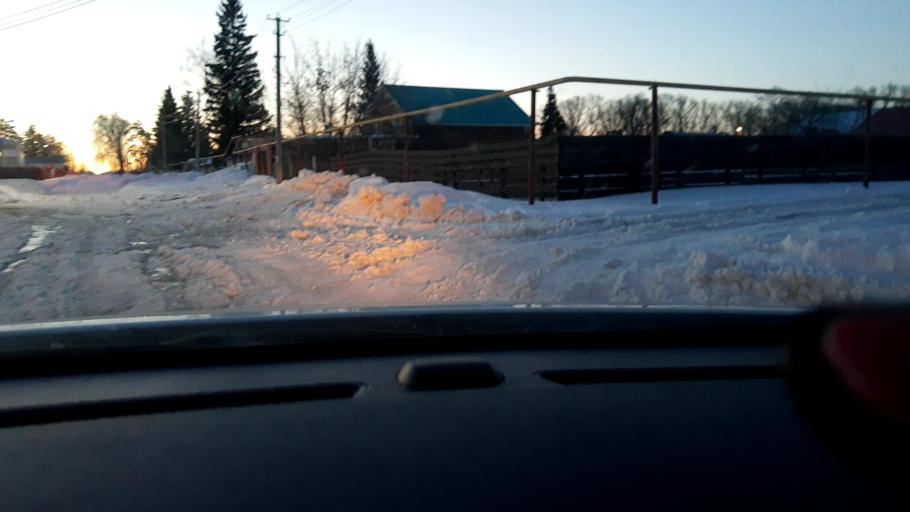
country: RU
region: Bashkortostan
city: Avdon
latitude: 54.3859
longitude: 55.6950
